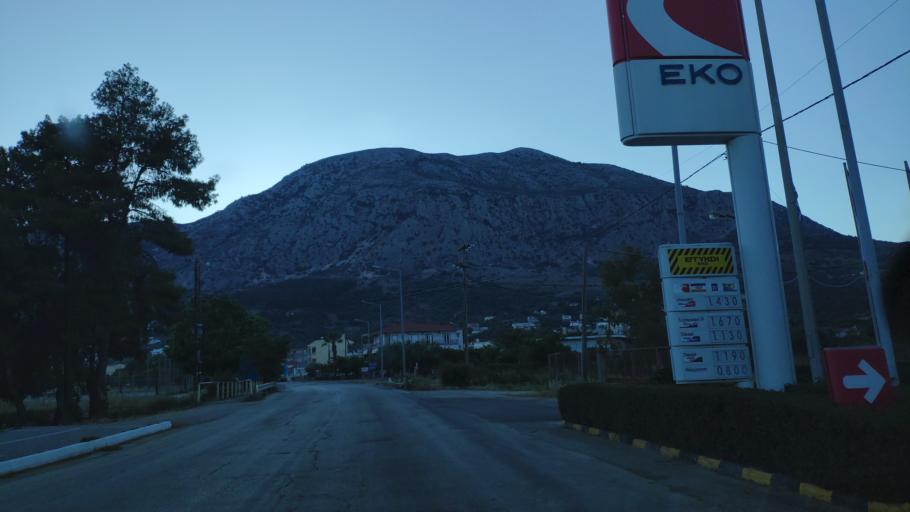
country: GR
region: West Greece
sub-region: Nomos Aitolias kai Akarnanias
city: Astakos
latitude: 38.5348
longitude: 21.0906
